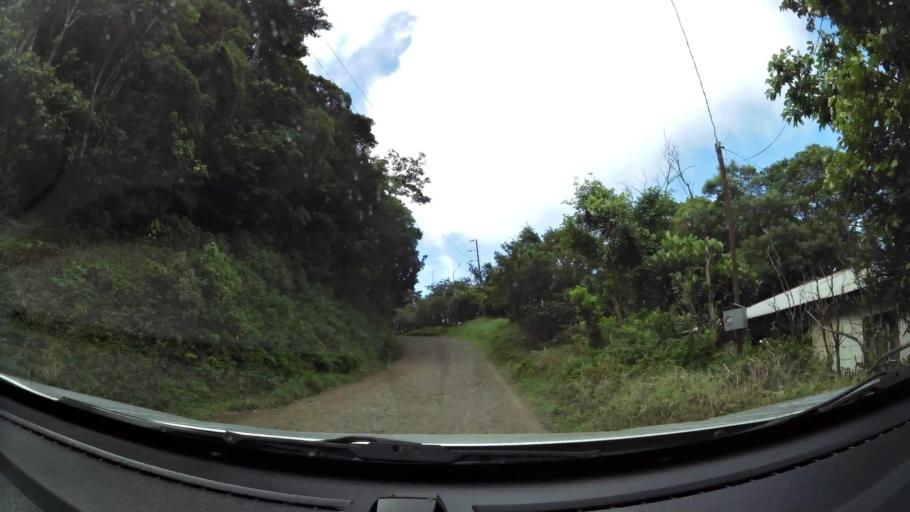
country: CR
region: Guanacaste
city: Juntas
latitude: 10.3467
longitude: -84.9122
